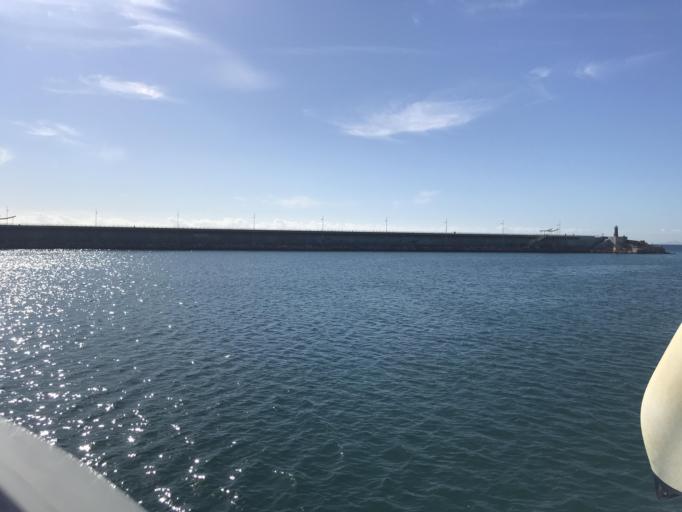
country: ES
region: Valencia
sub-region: Provincia de Alicante
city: Torrevieja
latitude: 37.9676
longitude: -0.6869
